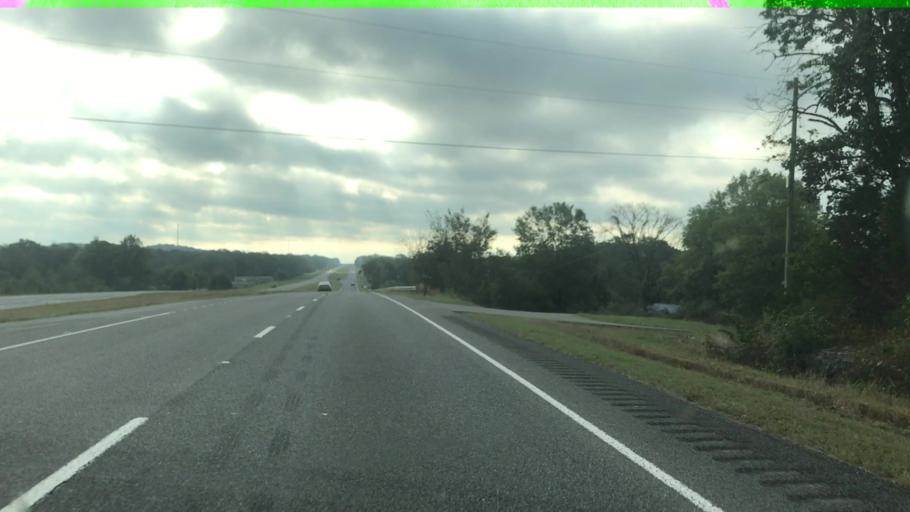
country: US
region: Alabama
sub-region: Morgan County
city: Danville
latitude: 34.4133
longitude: -87.1556
